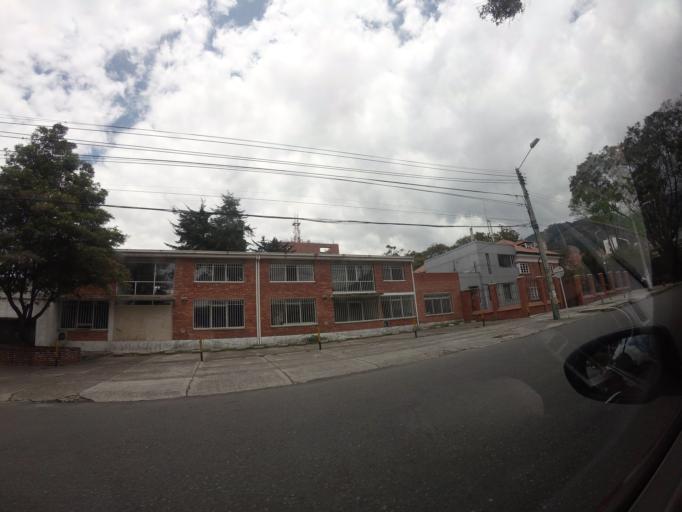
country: CO
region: Bogota D.C.
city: Barrio San Luis
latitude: 4.6603
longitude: -74.0573
